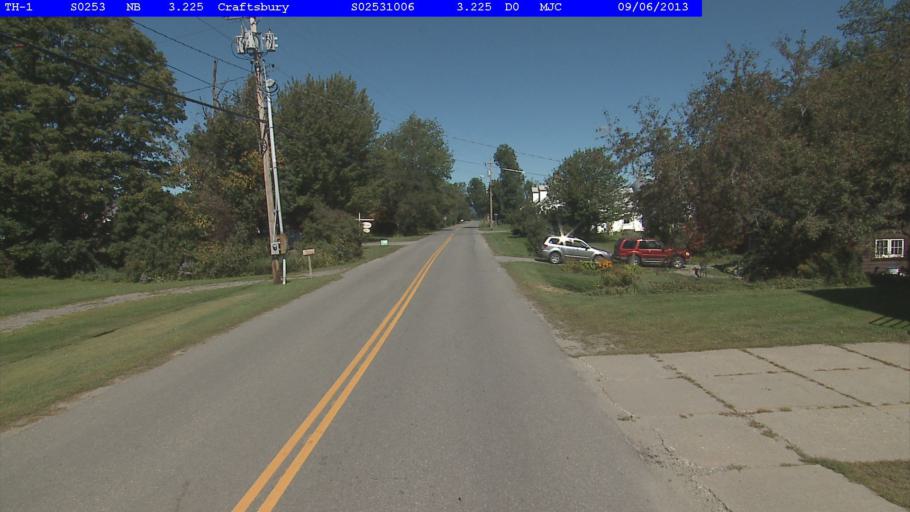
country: US
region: Vermont
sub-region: Caledonia County
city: Hardwick
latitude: 44.6546
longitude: -72.3823
